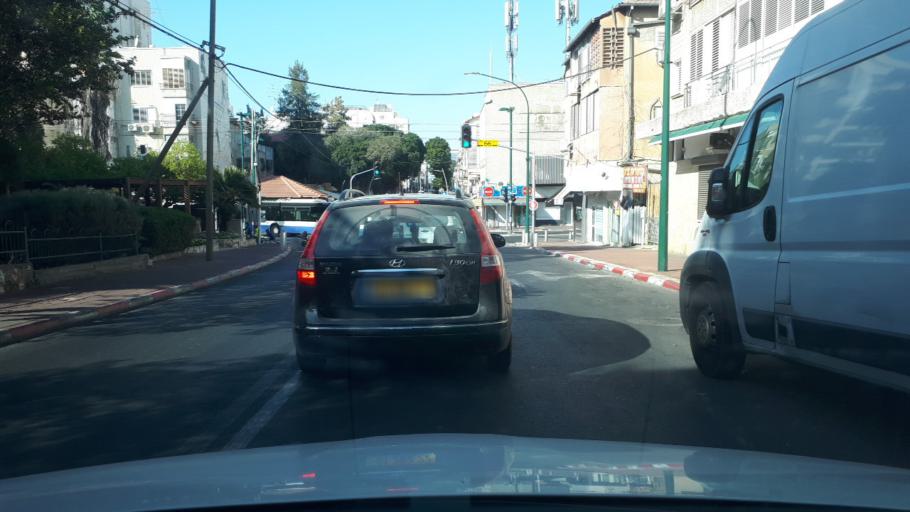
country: IL
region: Tel Aviv
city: Giv`atayim
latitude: 32.0741
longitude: 34.8230
